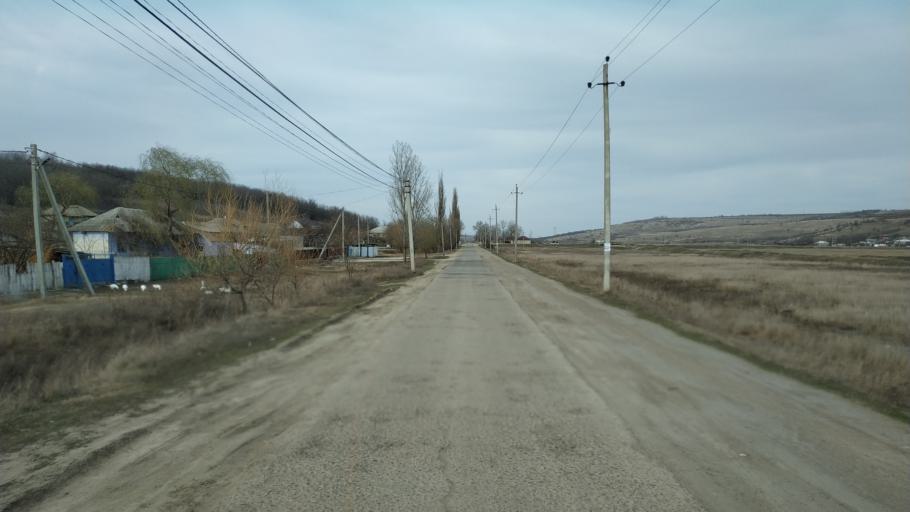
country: RO
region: Vaslui
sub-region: Comuna Dranceni
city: Dranceni
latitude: 46.8684
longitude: 28.1995
